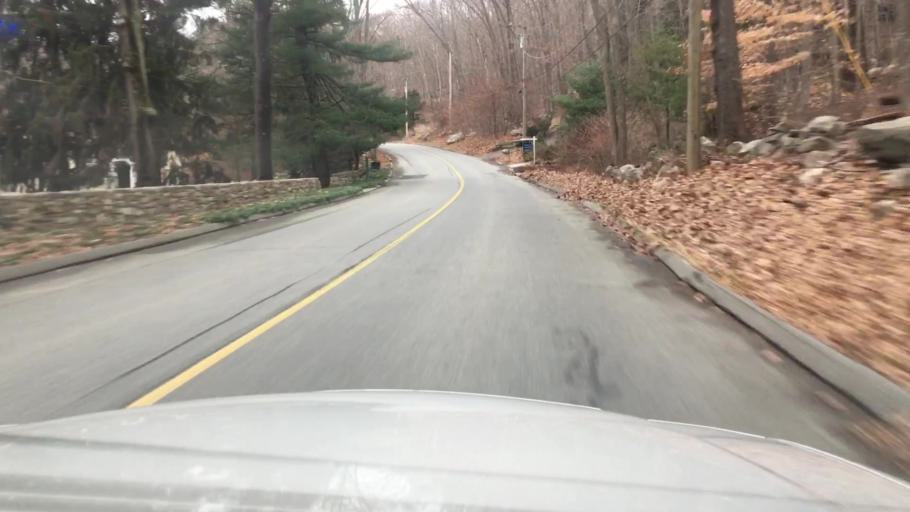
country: US
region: Connecticut
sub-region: Middlesex County
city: Essex Village
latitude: 41.3684
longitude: -72.4020
